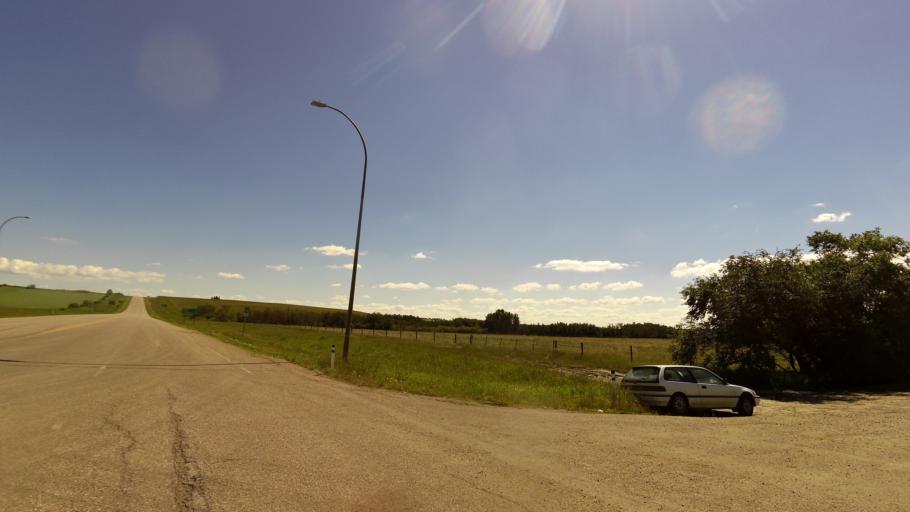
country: CA
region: Saskatchewan
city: Lloydminster
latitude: 52.8416
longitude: -110.0172
